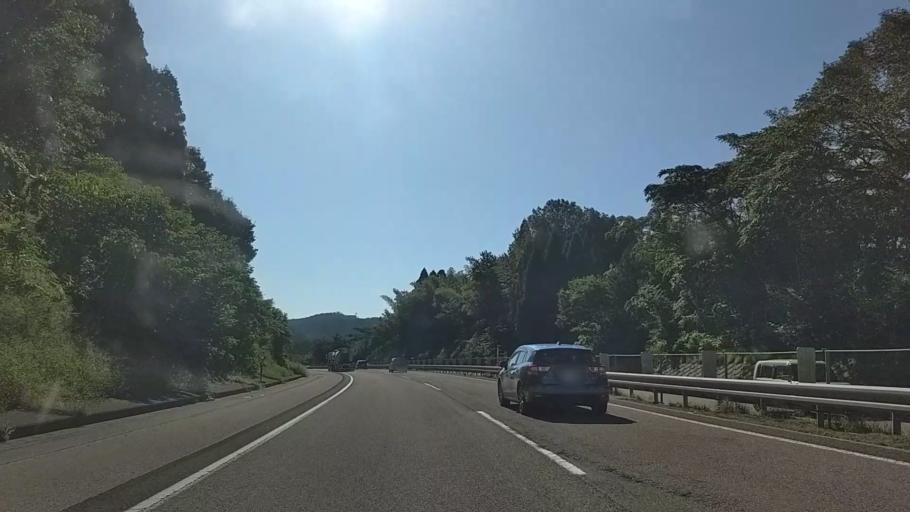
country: JP
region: Ishikawa
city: Tsubata
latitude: 36.5990
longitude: 136.7341
